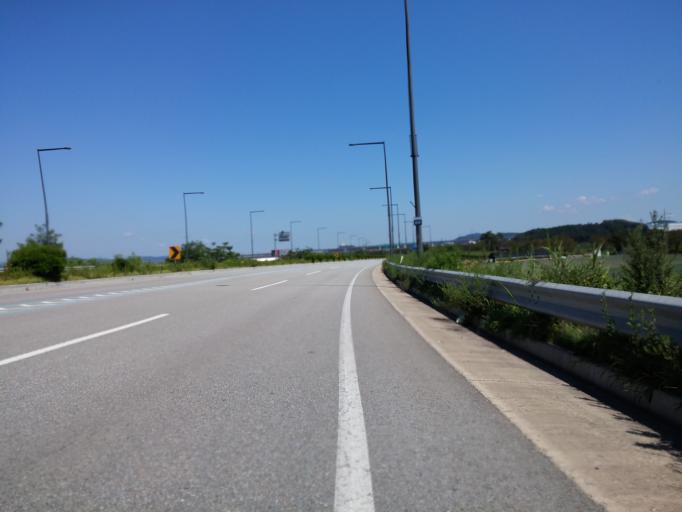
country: KR
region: Daejeon
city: Songgang-dong
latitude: 36.5890
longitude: 127.3243
